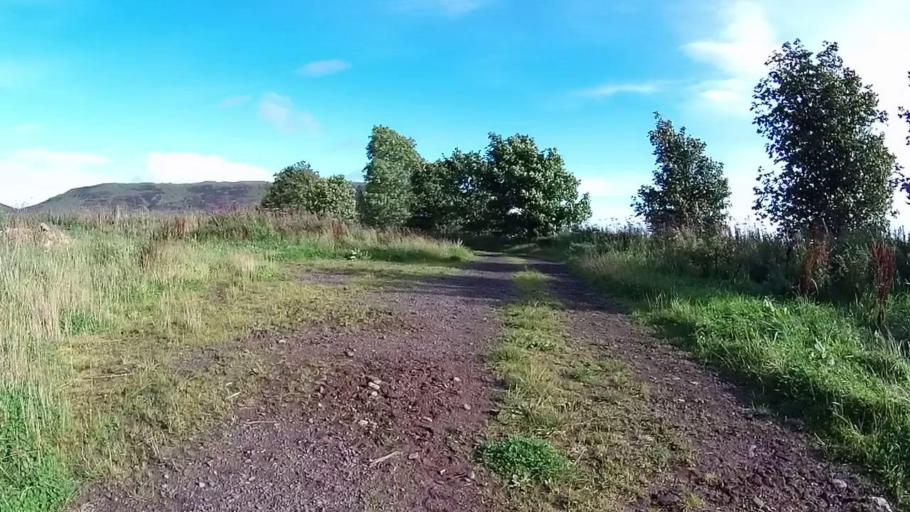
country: GB
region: Scotland
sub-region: Perth and Kinross
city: Milnathort
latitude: 56.2352
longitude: -3.3514
